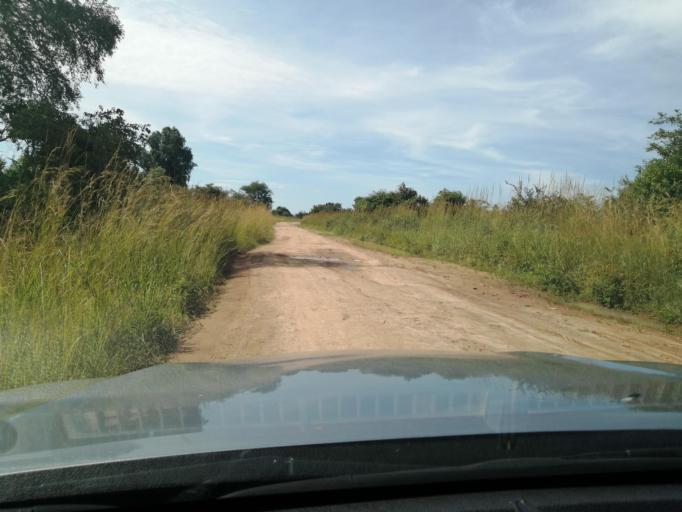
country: ZM
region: Central
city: Chibombo
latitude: -14.9518
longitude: 27.8029
